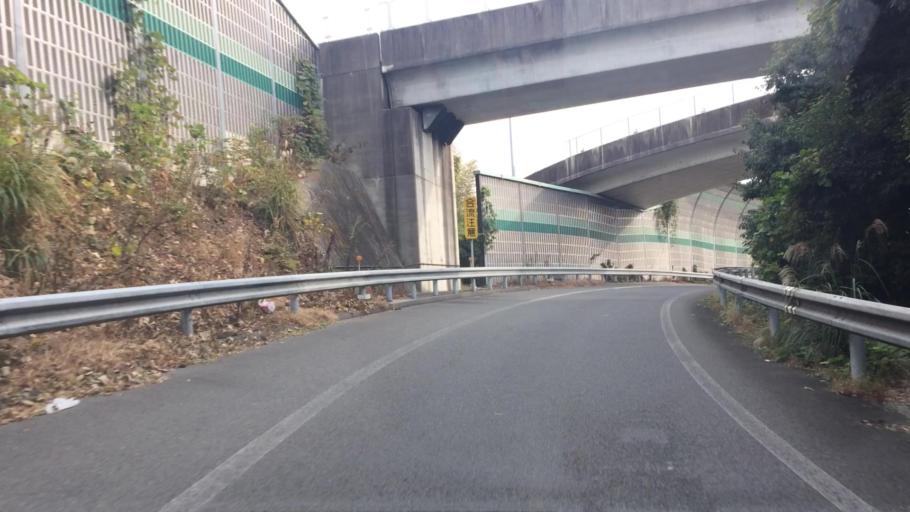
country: JP
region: Kanagawa
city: Yokohama
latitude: 35.5460
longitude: 139.6039
